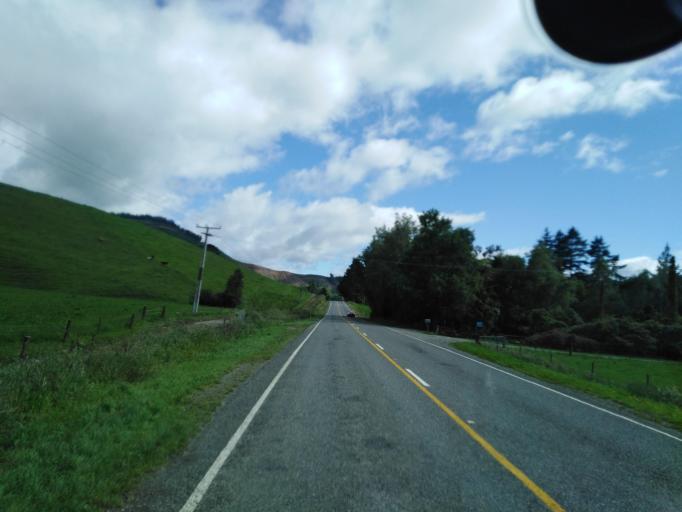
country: NZ
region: Nelson
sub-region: Nelson City
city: Nelson
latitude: -41.2760
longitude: 173.5731
